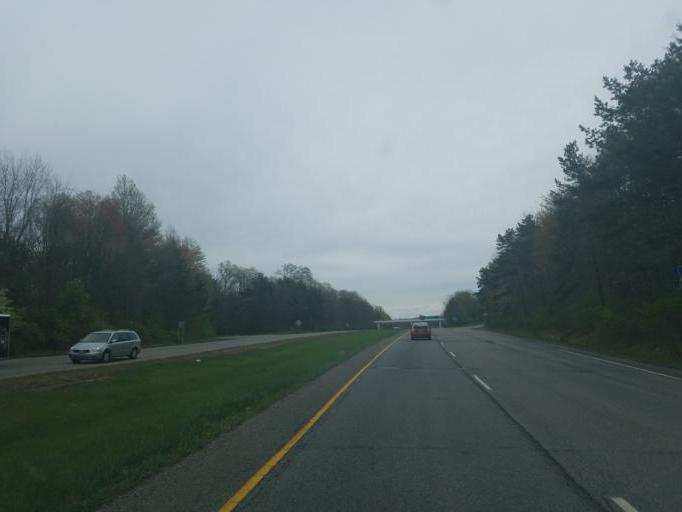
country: US
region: Ohio
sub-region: Wayne County
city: Doylestown
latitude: 40.9909
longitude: -81.6725
